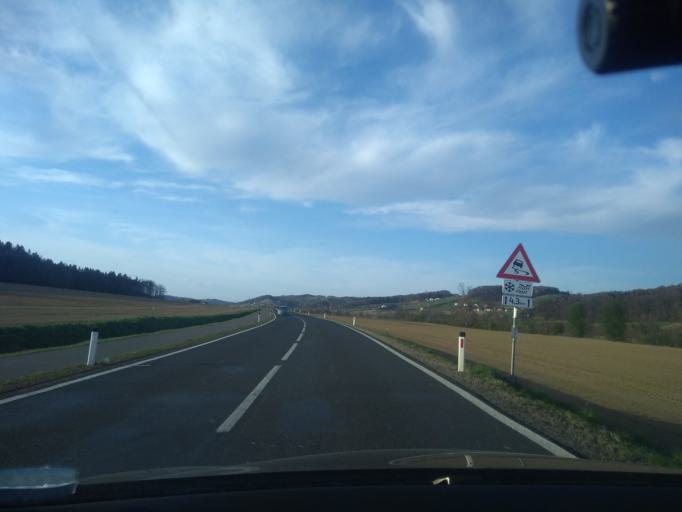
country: AT
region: Styria
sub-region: Politischer Bezirk Suedoststeiermark
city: Jagerberg
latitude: 46.8733
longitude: 15.7261
